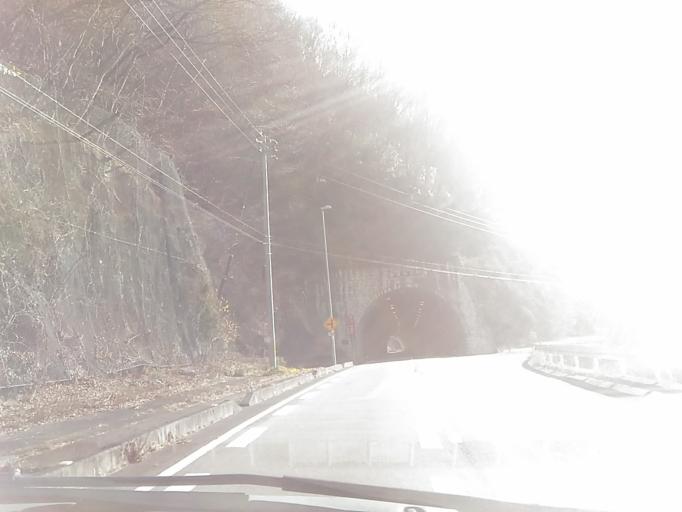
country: JP
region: Fukushima
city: Iwaki
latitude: 37.0048
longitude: 140.6997
